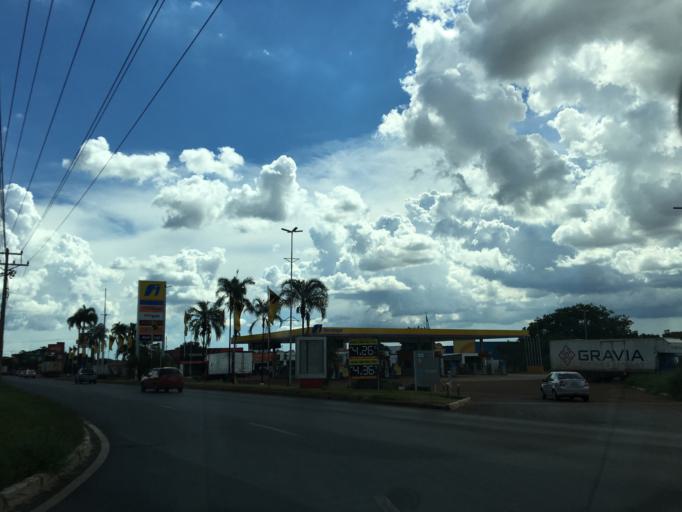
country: BR
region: Federal District
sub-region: Brasilia
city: Brasilia
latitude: -15.7921
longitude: -47.9442
